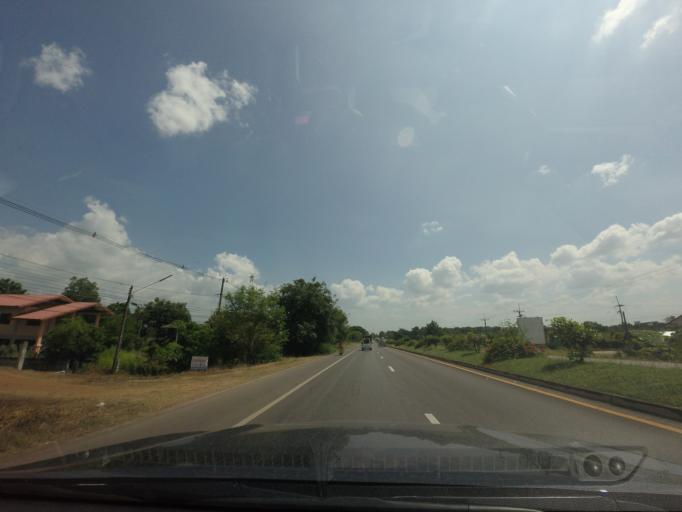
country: TH
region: Phetchabun
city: Nong Phai
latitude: 16.1042
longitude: 101.0434
